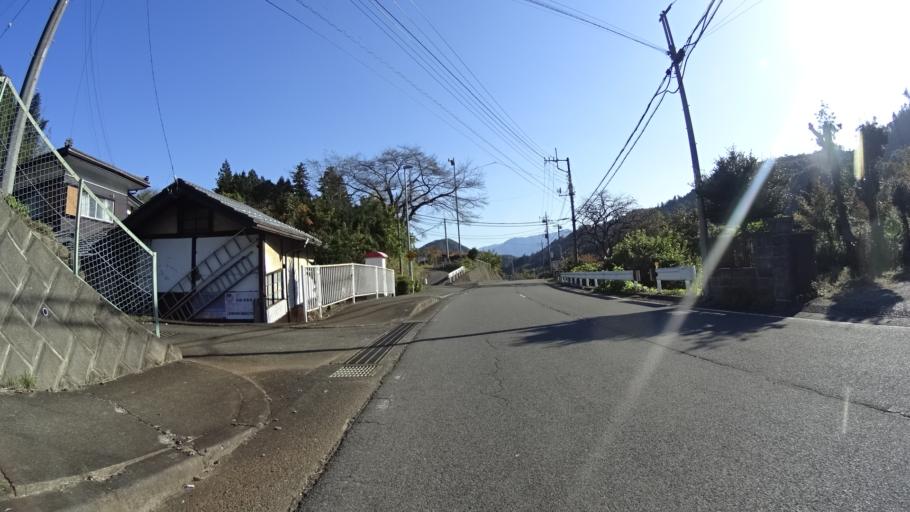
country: JP
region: Yamanashi
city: Uenohara
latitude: 35.6511
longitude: 139.1212
